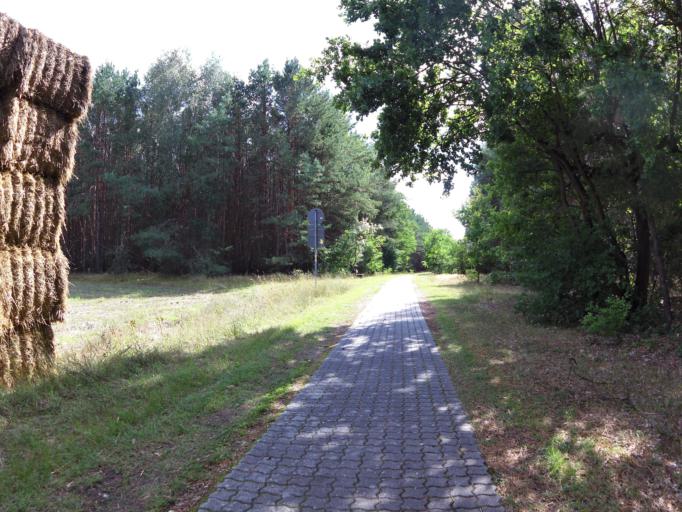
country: DE
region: Brandenburg
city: Storkow
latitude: 52.2278
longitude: 13.8740
